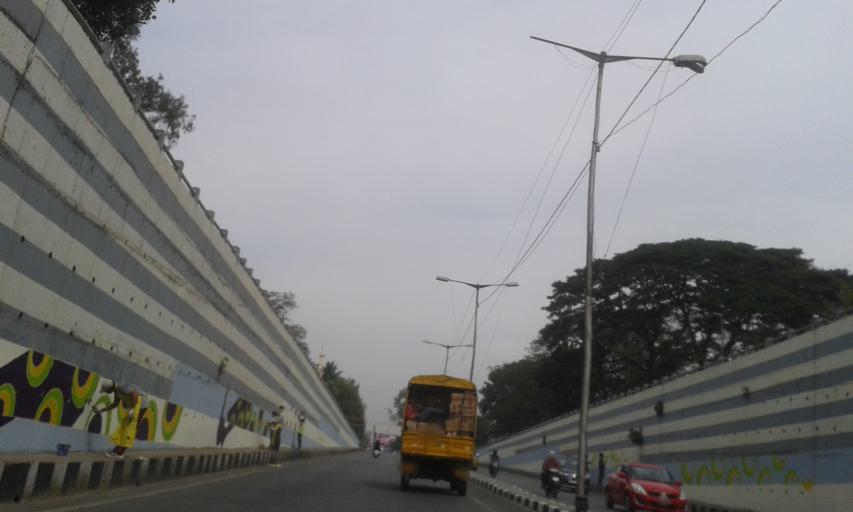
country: IN
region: Karnataka
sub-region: Bangalore Urban
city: Bangalore
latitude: 12.9368
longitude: 77.6018
